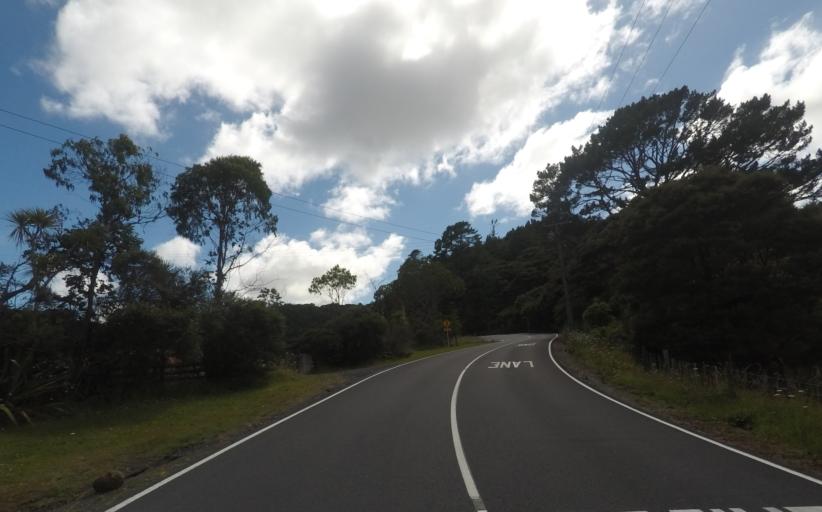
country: NZ
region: Auckland
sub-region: Auckland
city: Muriwai Beach
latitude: -36.8663
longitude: 174.5055
